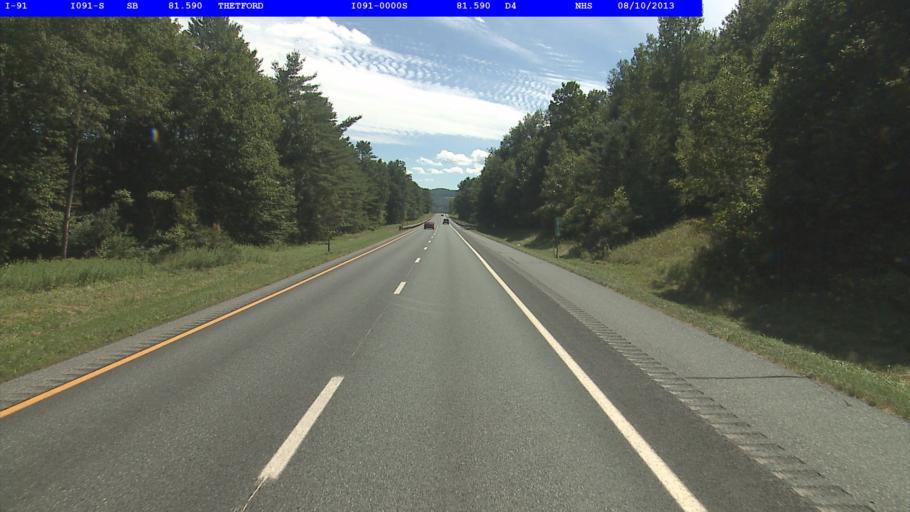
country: US
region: New Hampshire
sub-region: Grafton County
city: Lyme
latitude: 43.7773
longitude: -72.2222
